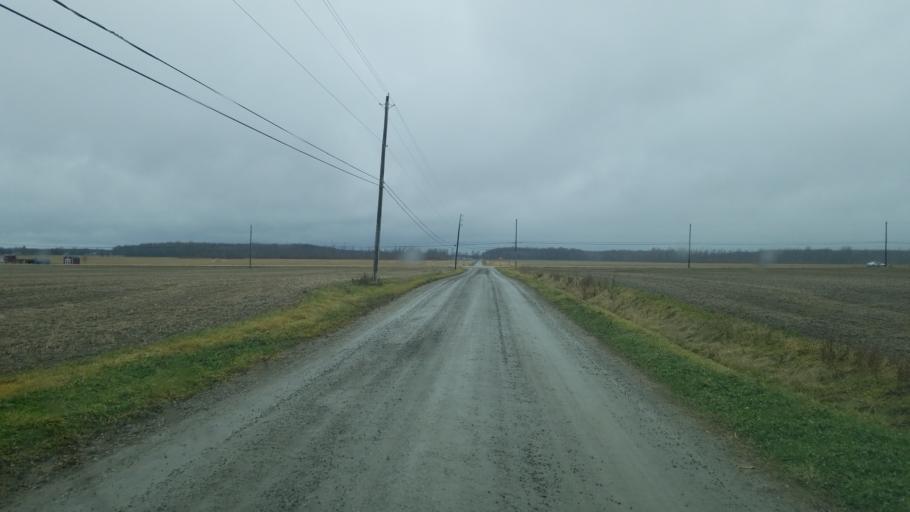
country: US
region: Ohio
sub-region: Ashtabula County
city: Roaming Shores
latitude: 41.6048
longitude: -80.7050
